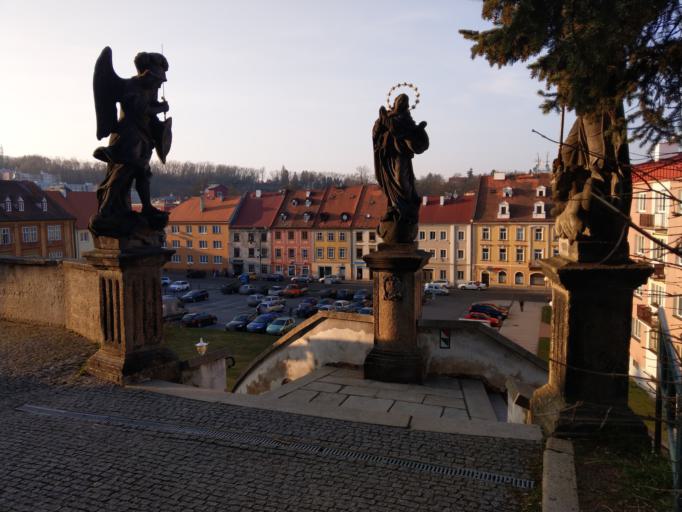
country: CZ
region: Karlovarsky
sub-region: Okres Cheb
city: Cheb
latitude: 50.0809
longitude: 12.3711
